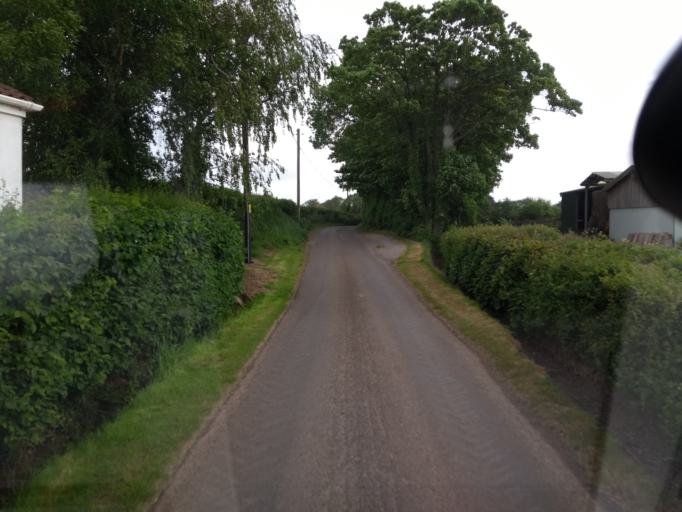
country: GB
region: England
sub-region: Somerset
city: North Petherton
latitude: 51.1378
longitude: -3.1037
